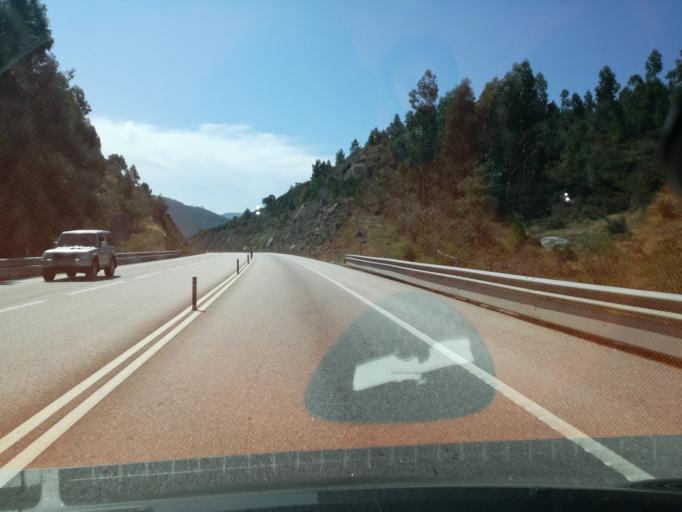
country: PT
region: Viana do Castelo
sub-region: Vila Nova de Cerveira
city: Vila Nova de Cerveira
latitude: 41.9008
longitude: -8.7870
